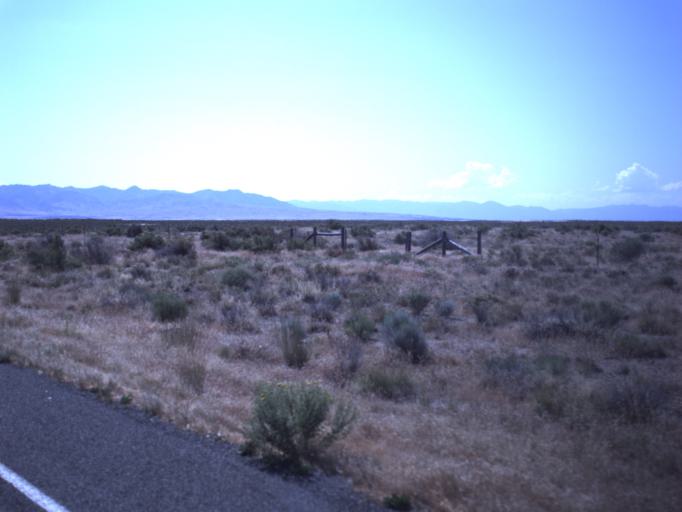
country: US
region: Utah
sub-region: Millard County
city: Delta
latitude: 39.4859
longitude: -112.5360
